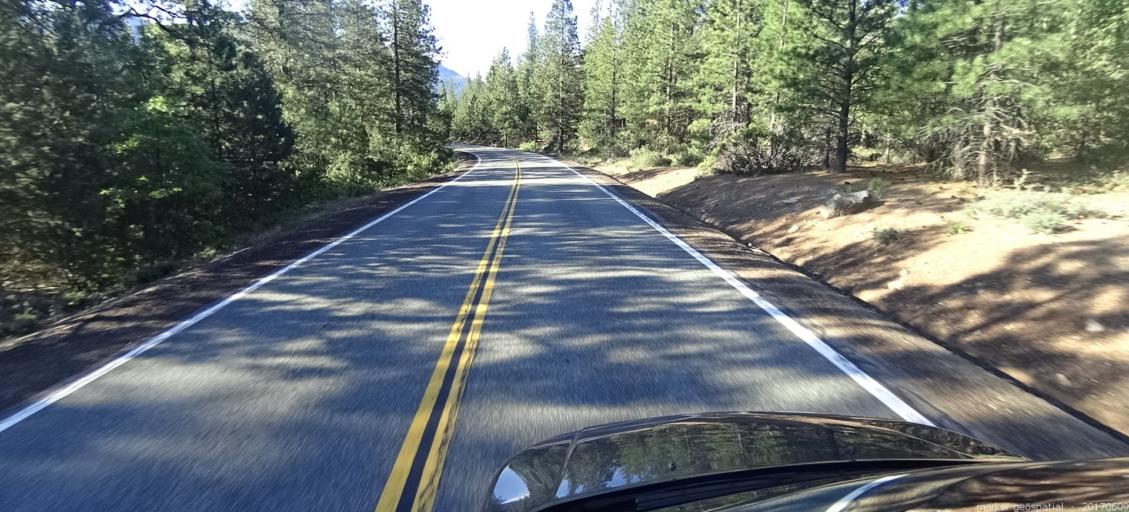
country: US
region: California
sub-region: Siskiyou County
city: Weed
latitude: 41.4311
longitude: -122.6387
